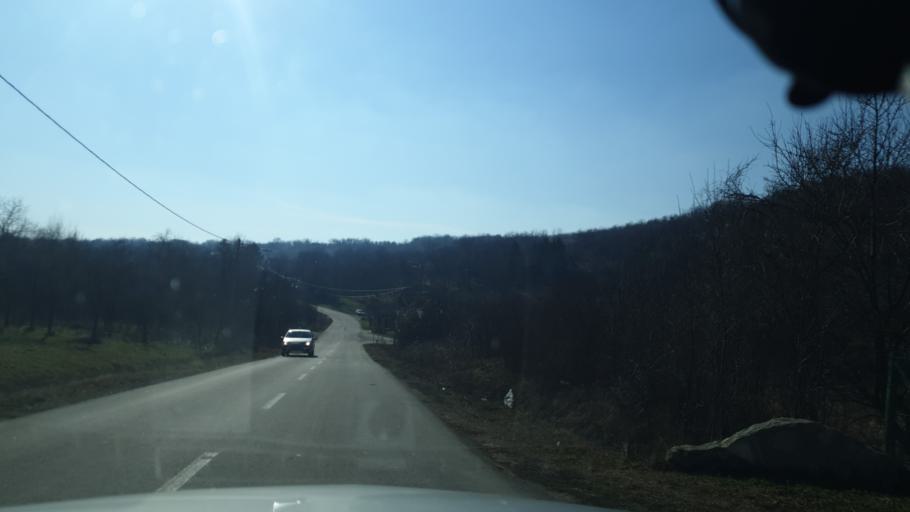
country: RS
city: Vrdnik
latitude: 45.1112
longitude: 19.7675
